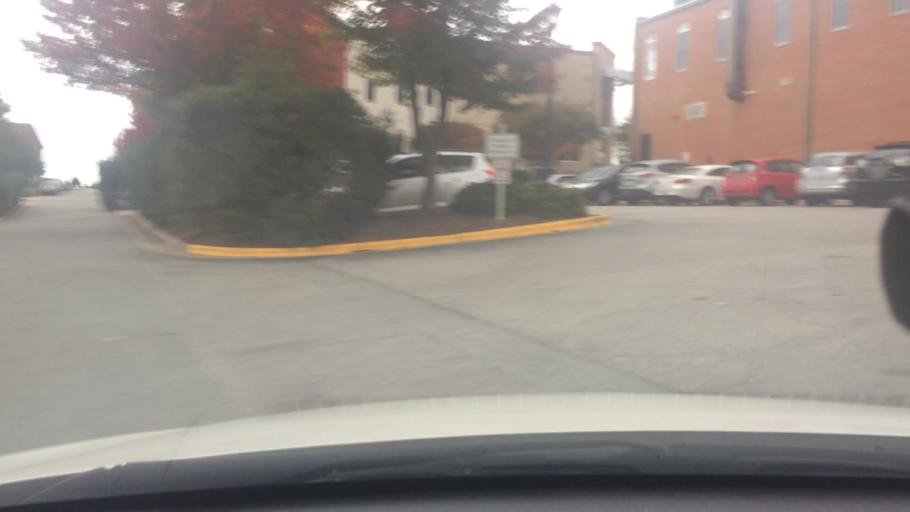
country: US
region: North Carolina
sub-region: Orange County
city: Carrboro
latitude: 35.8802
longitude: -79.0666
